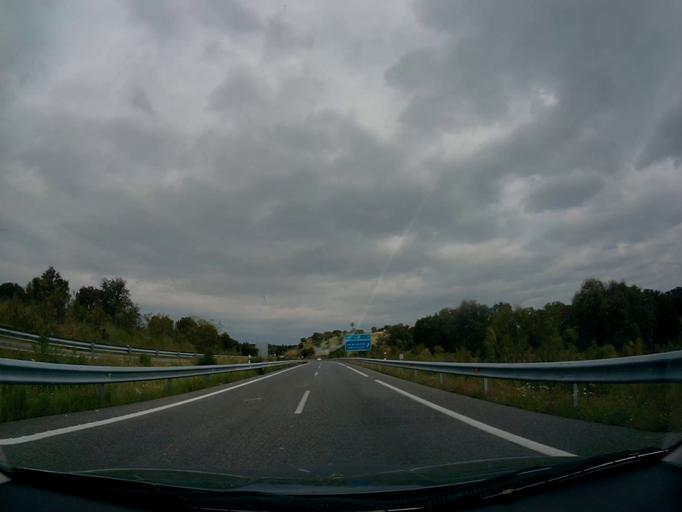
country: ES
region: Madrid
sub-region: Provincia de Madrid
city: Villaviciosa de Odon
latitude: 40.3735
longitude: -3.9509
